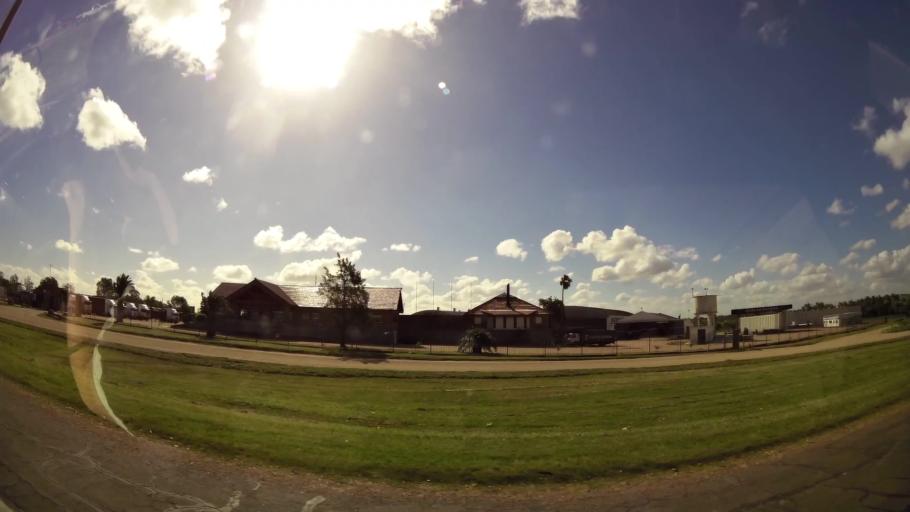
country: UY
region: Canelones
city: La Paz
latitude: -34.8316
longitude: -56.2531
